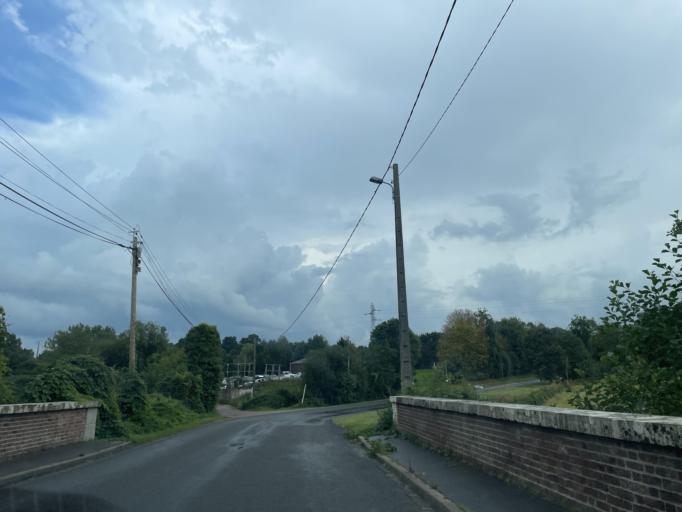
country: FR
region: Haute-Normandie
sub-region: Departement de la Seine-Maritime
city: Neufchatel-en-Bray
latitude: 49.7233
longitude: 1.4347
